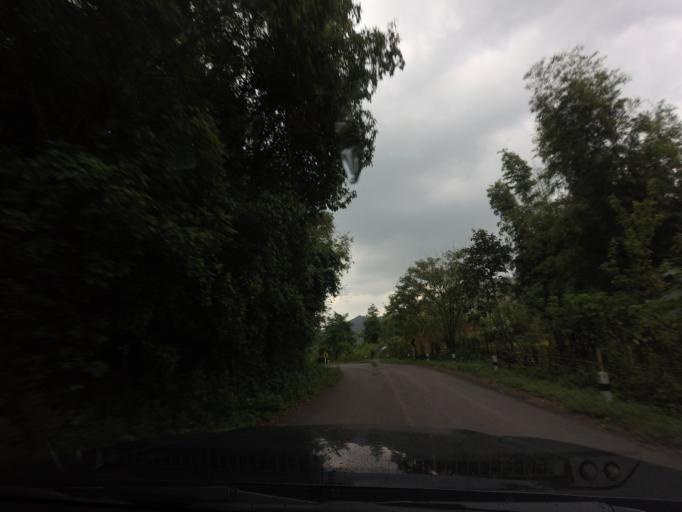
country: TH
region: Nan
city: Bo Kluea
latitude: 19.3337
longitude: 101.1663
